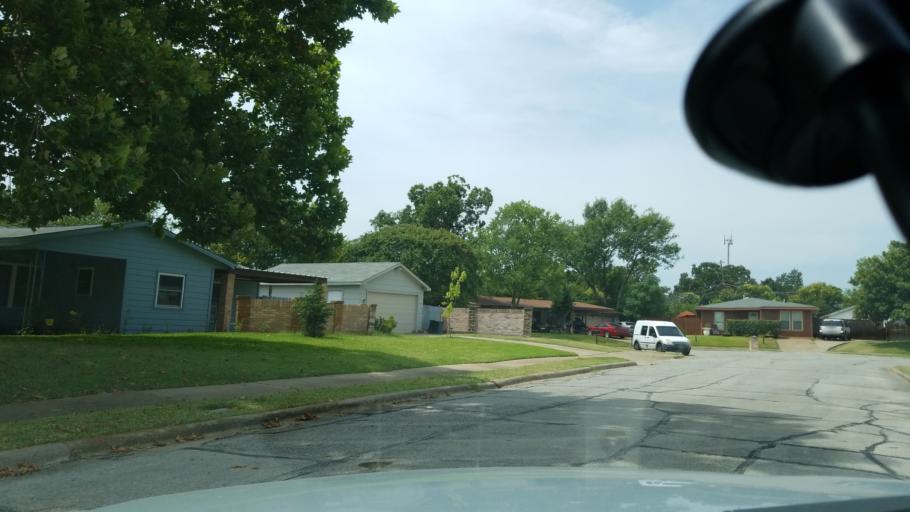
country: US
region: Texas
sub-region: Dallas County
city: Irving
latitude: 32.8301
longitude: -96.9878
